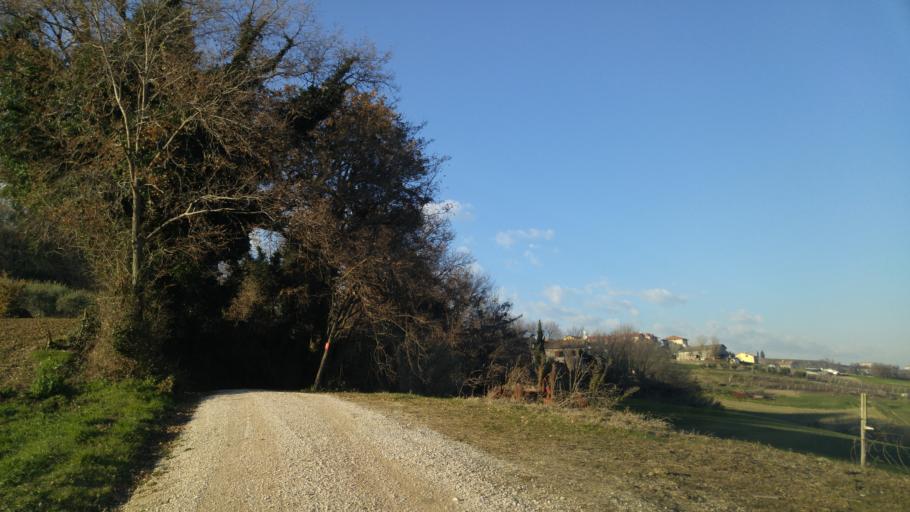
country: IT
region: The Marches
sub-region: Provincia di Pesaro e Urbino
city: Piagge
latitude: 43.7313
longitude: 12.9704
